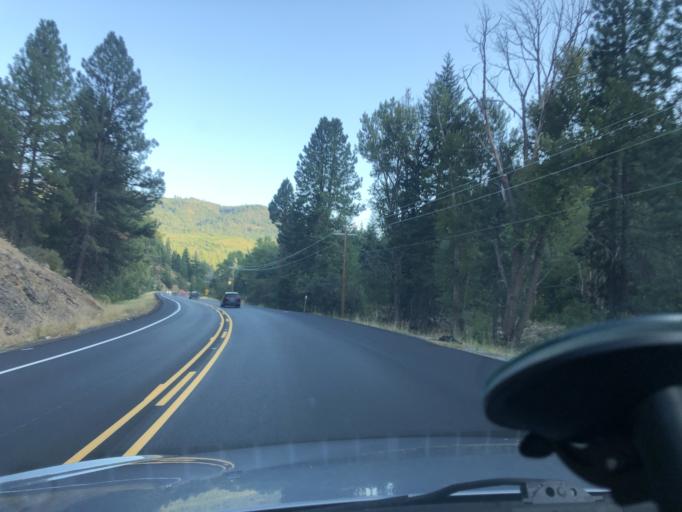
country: US
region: Washington
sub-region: Kittitas County
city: Cle Elum
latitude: 47.2147
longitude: -120.7006
